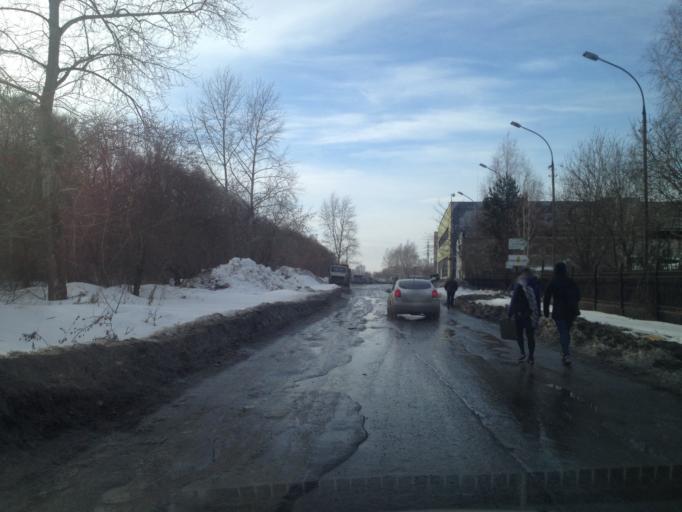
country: RU
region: Sverdlovsk
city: Yekaterinburg
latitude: 56.8170
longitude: 60.6790
